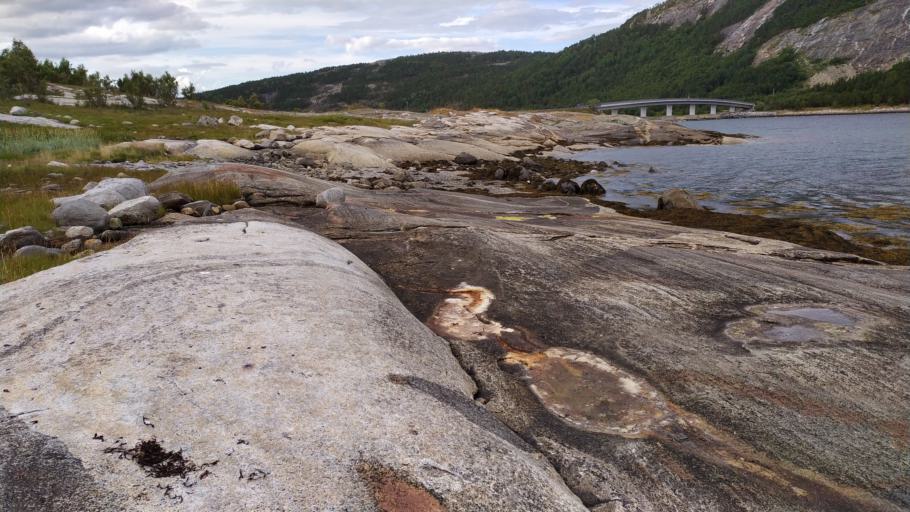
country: NO
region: Nordland
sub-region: Bodo
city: Loding
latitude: 67.1941
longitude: 14.6299
